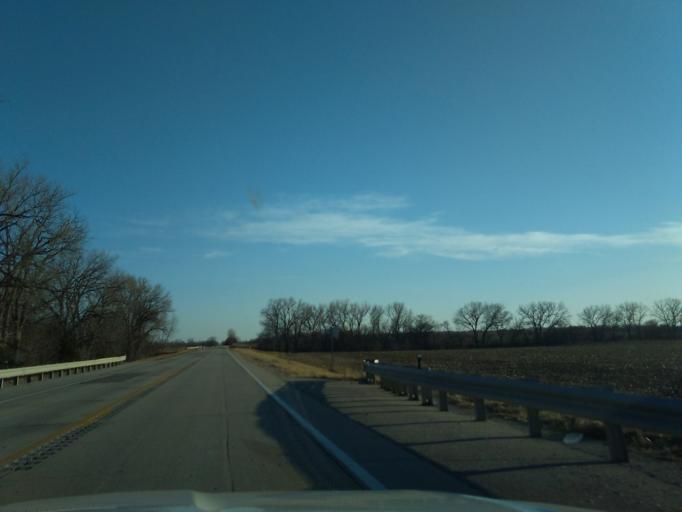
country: US
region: Nebraska
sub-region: Johnson County
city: Tecumseh
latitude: 40.5048
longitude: -96.1798
